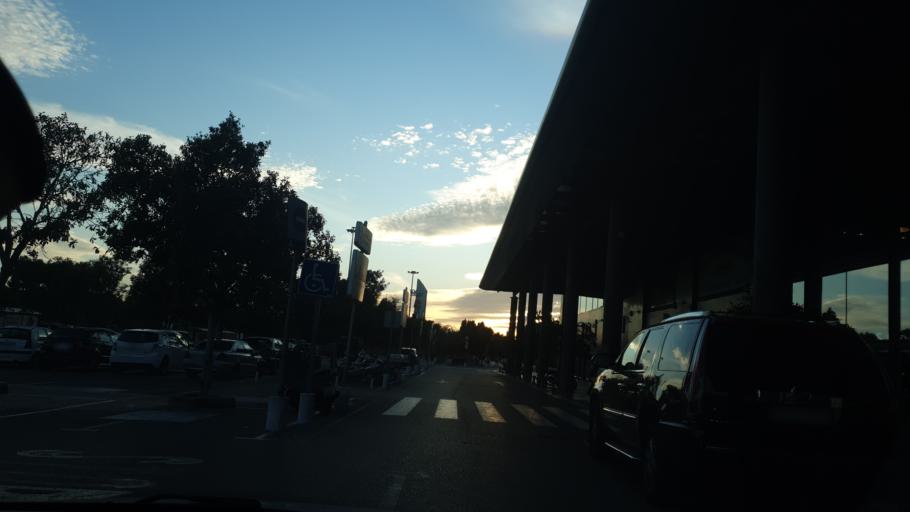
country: ES
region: Andalusia
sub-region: Provincia de Malaga
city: Marbella
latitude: 36.5214
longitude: -4.8738
